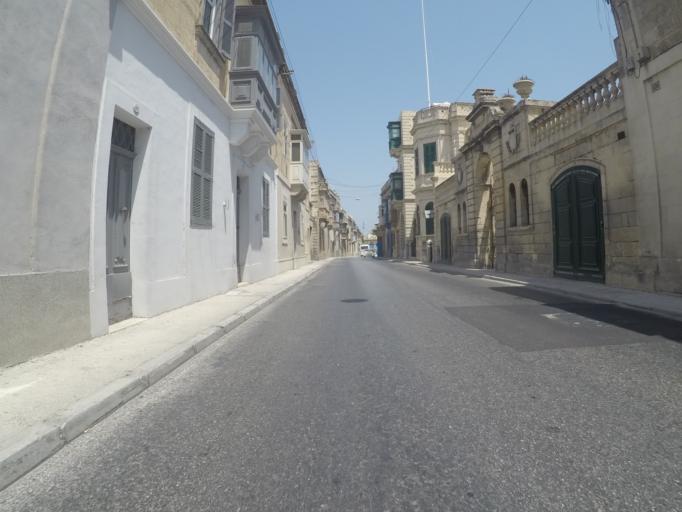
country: MT
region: Ir-Rabat
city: Rabat
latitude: 35.8791
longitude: 14.4008
